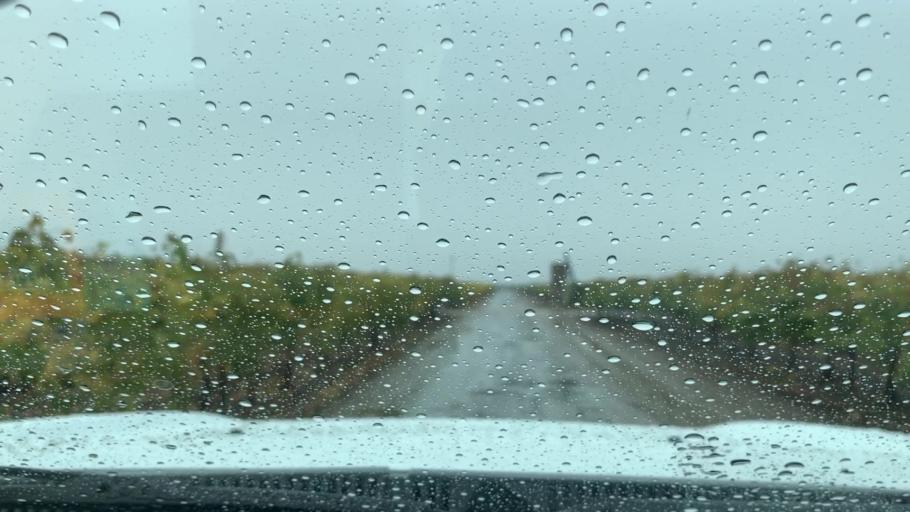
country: US
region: California
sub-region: Tulare County
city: Richgrove
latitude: 35.8378
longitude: -119.1672
